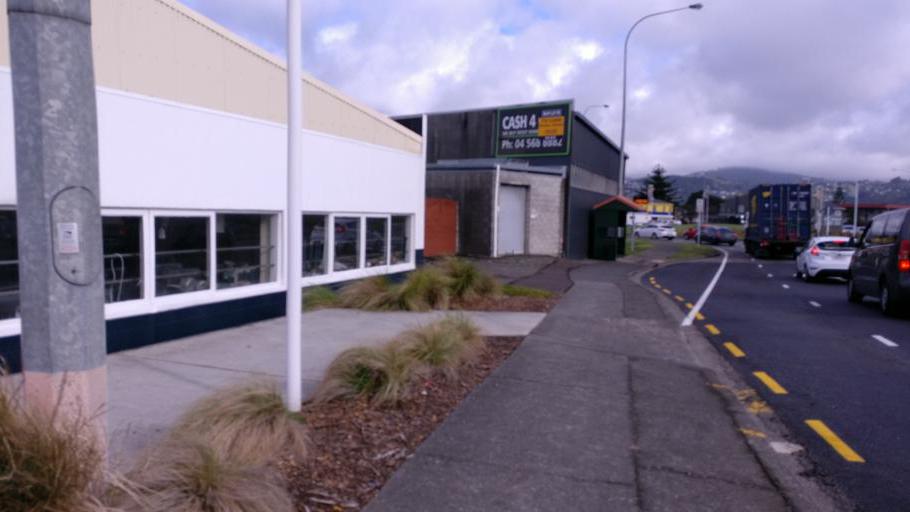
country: NZ
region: Wellington
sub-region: Lower Hutt City
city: Lower Hutt
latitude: -41.2348
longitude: 174.9047
